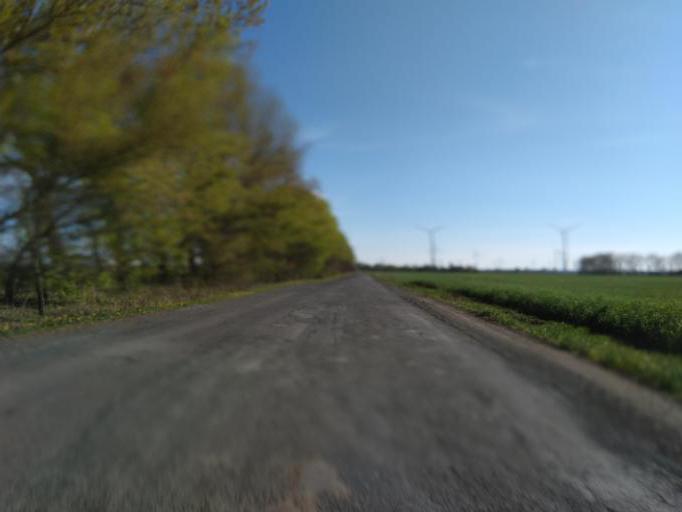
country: DE
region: Brandenburg
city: Neutrebbin
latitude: 52.7237
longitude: 14.2138
